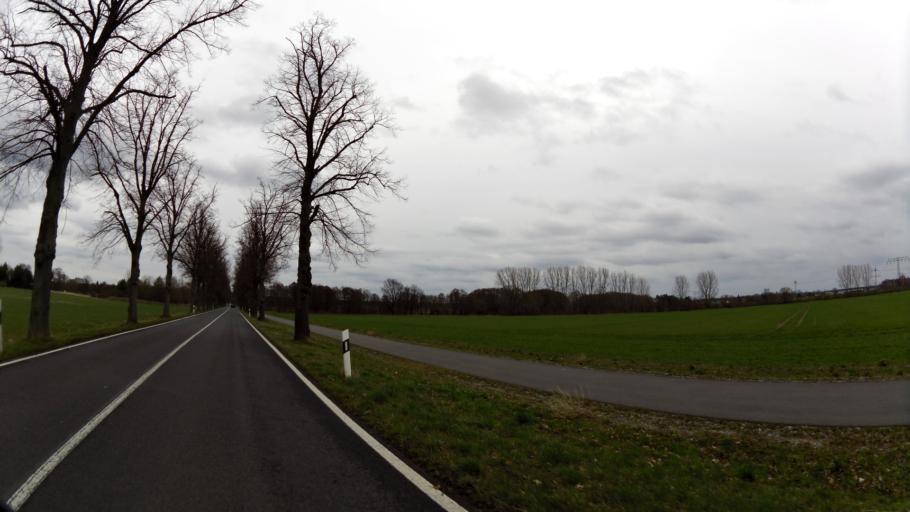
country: DE
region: Brandenburg
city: Schonefeld
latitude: 52.3472
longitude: 13.5404
